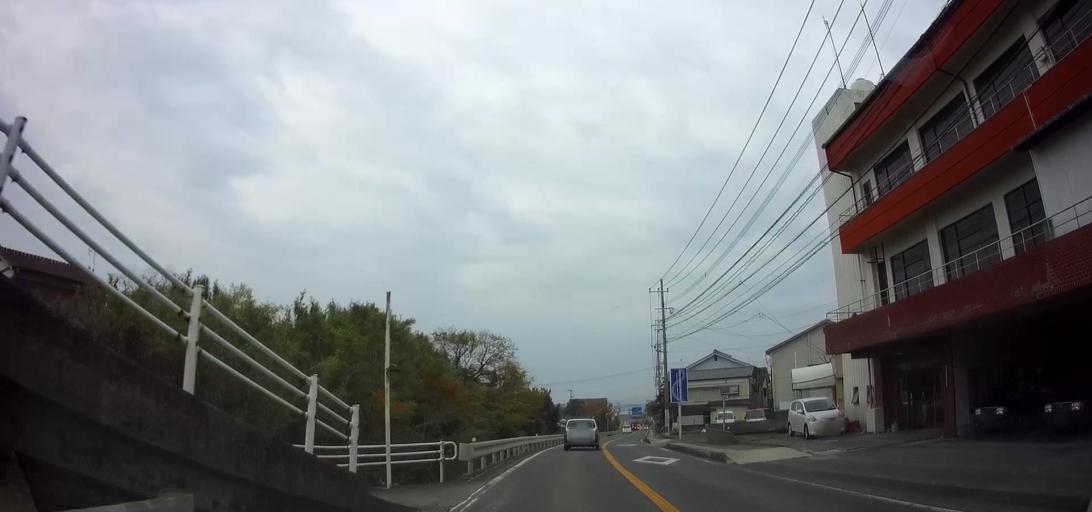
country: JP
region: Nagasaki
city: Shimabara
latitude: 32.6554
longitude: 130.2912
